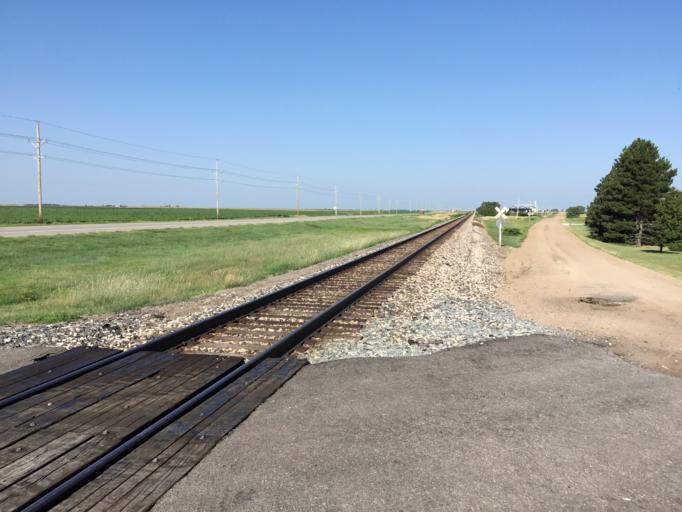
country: US
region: Kansas
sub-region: Pratt County
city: Pratt
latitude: 37.6301
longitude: -98.9305
